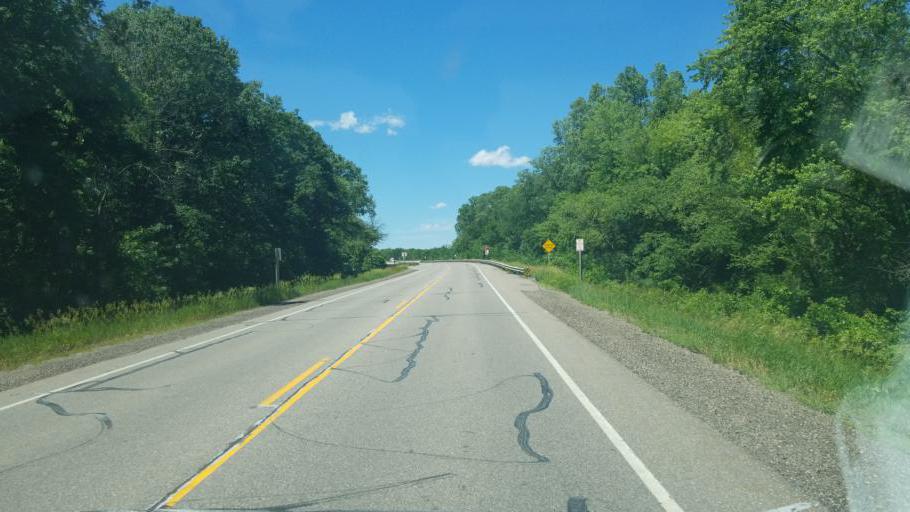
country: US
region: Wisconsin
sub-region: Adams County
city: Friendship
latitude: 44.0482
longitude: -90.0132
